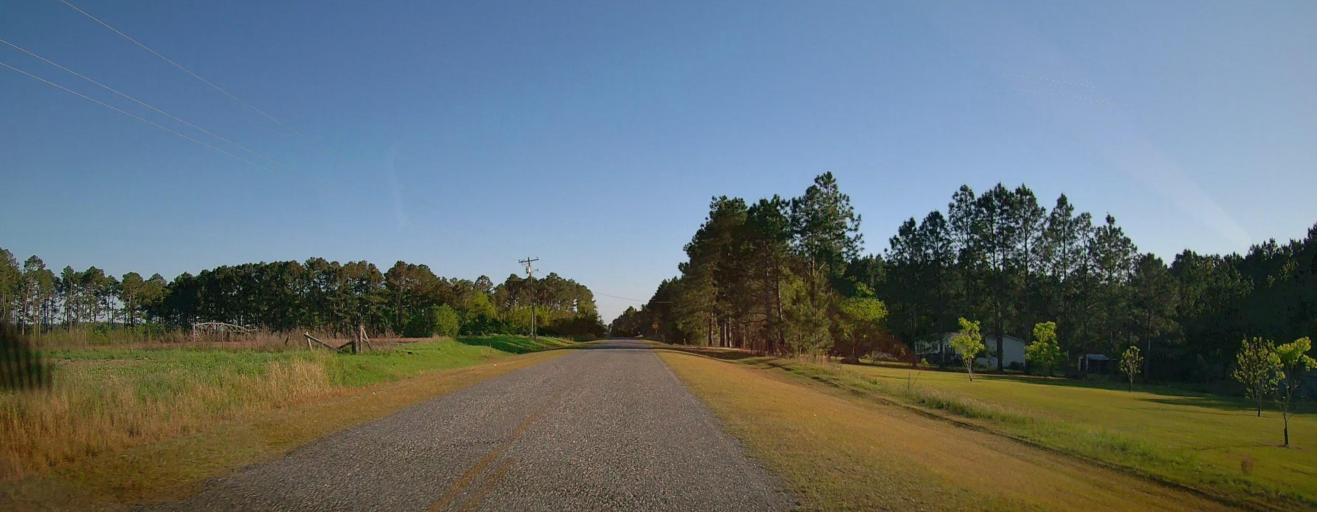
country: US
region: Georgia
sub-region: Ben Hill County
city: Fitzgerald
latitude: 31.6619
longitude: -83.1469
